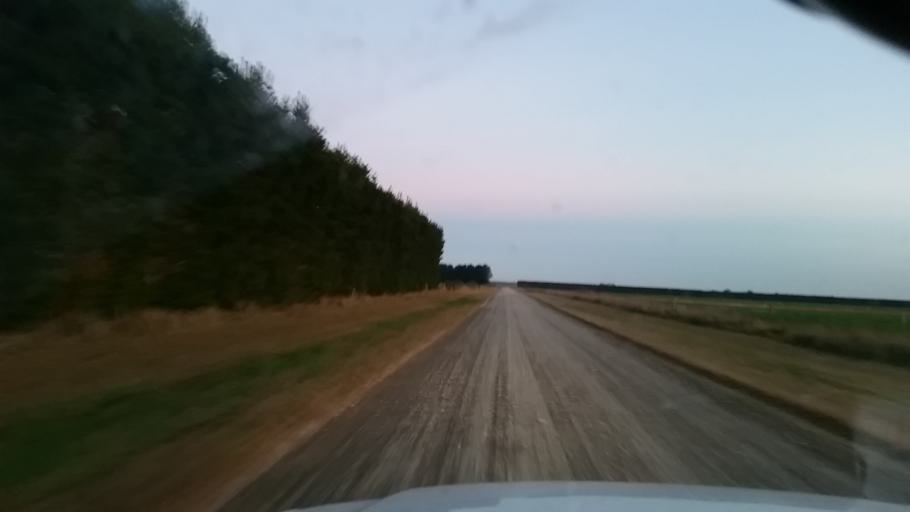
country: NZ
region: Canterbury
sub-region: Ashburton District
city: Tinwald
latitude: -43.9400
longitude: 171.6096
